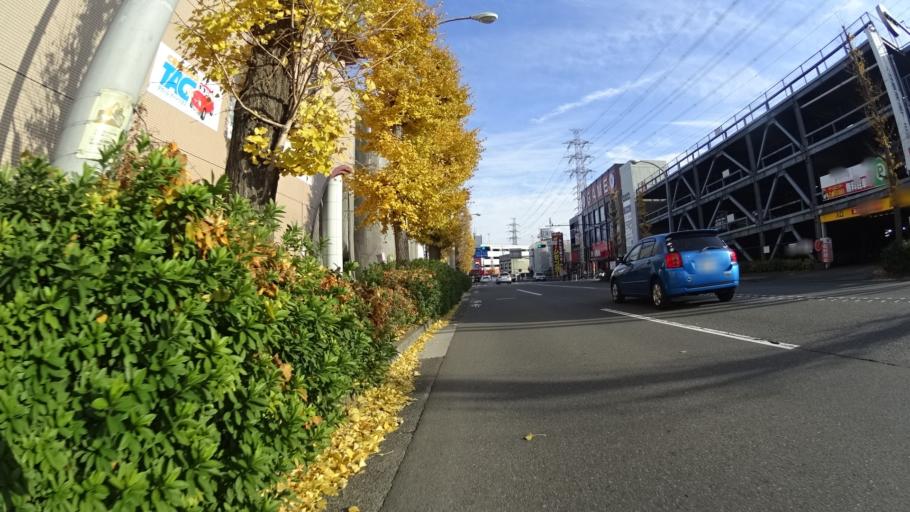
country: JP
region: Tokyo
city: Hino
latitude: 35.6658
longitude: 139.3658
